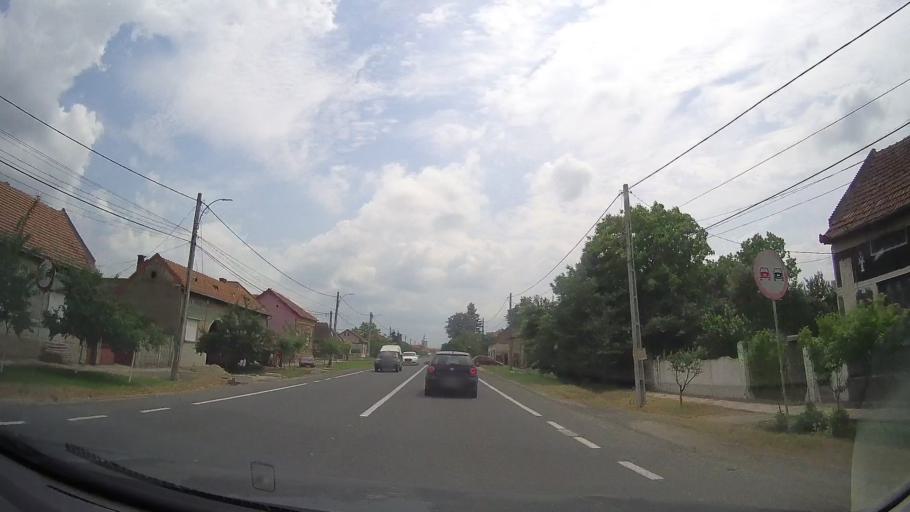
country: RO
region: Timis
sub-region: Comuna Costeiu
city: Costeiu
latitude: 45.7344
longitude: 21.8602
